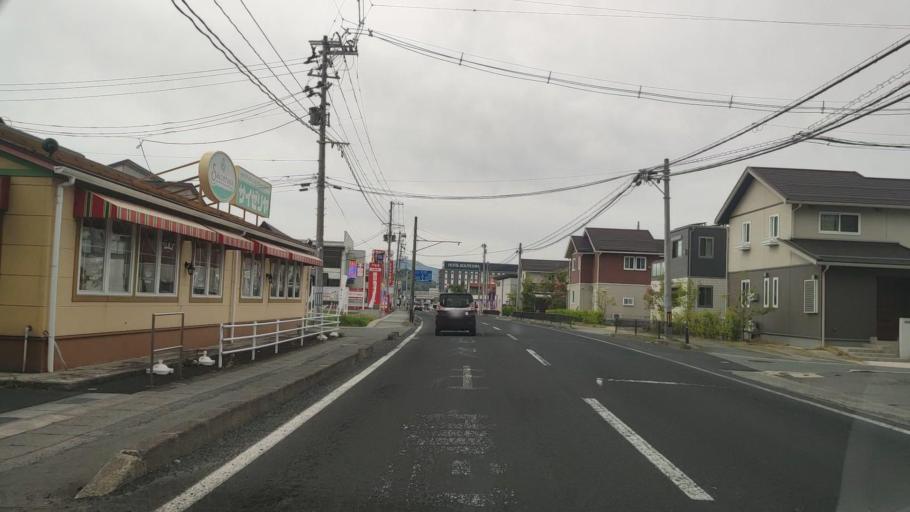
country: JP
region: Yamagata
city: Yamagata-shi
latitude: 38.2199
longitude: 140.3243
